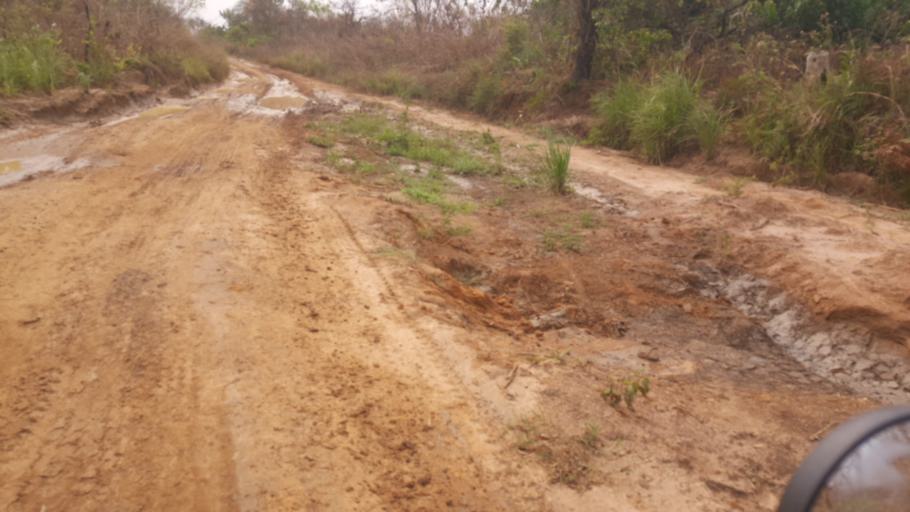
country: CD
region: Bandundu
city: Bandundu
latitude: -3.4542
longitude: 17.7478
